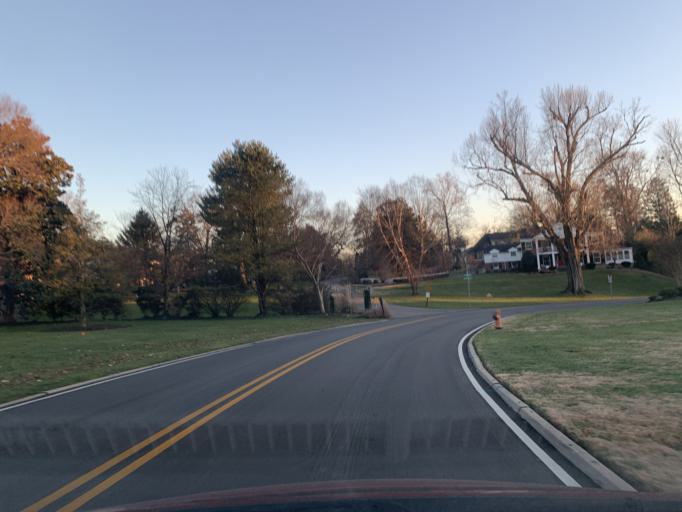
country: US
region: Kentucky
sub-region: Jefferson County
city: Saint Matthews
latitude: 38.2372
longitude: -85.6813
